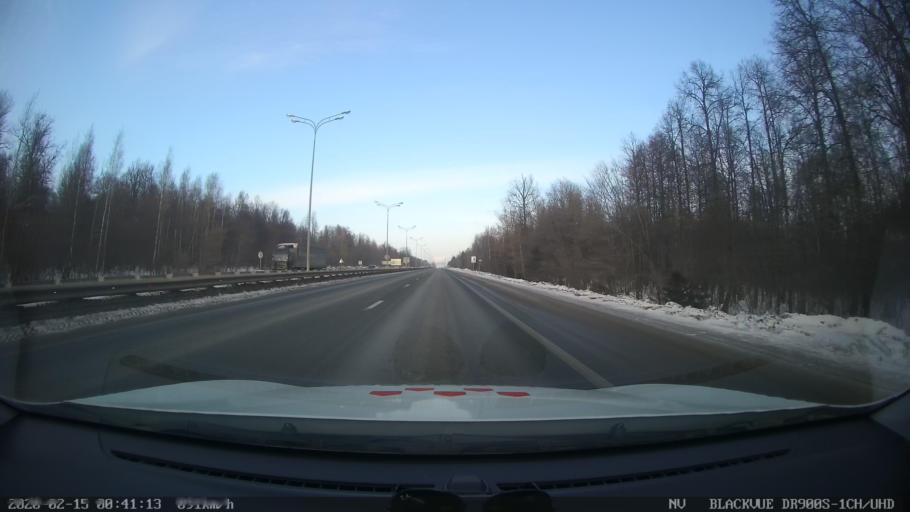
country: RU
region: Tatarstan
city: Sviyazhsk
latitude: 55.7453
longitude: 48.7940
